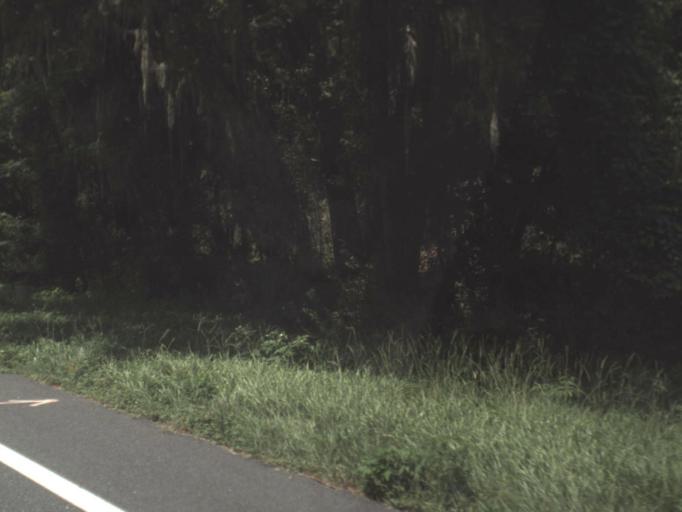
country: US
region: Florida
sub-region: Suwannee County
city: Wellborn
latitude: 30.3779
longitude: -82.8094
